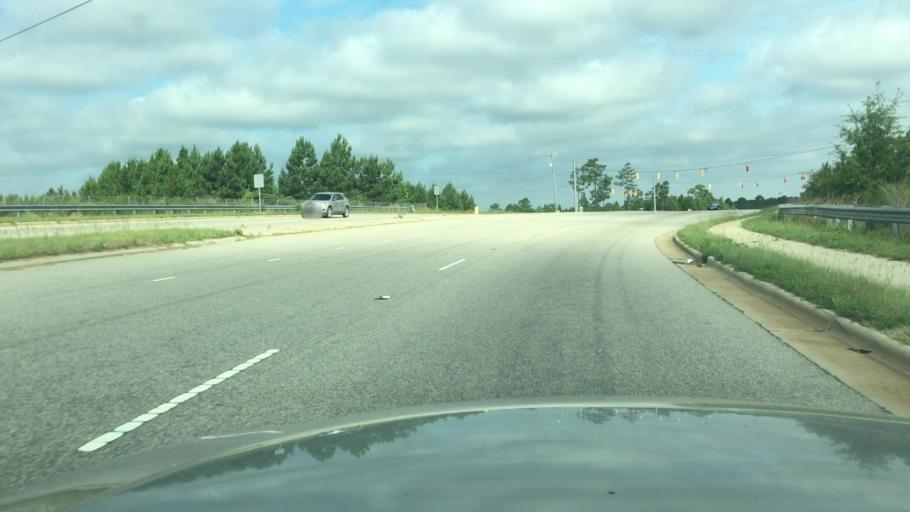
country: US
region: North Carolina
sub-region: Cumberland County
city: Hope Mills
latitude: 34.9903
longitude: -78.9471
